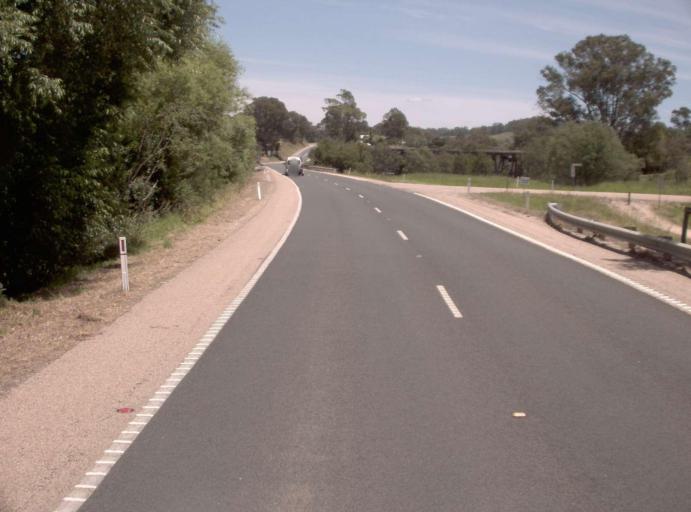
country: AU
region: Victoria
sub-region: East Gippsland
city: Bairnsdale
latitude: -37.7103
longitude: 147.8145
